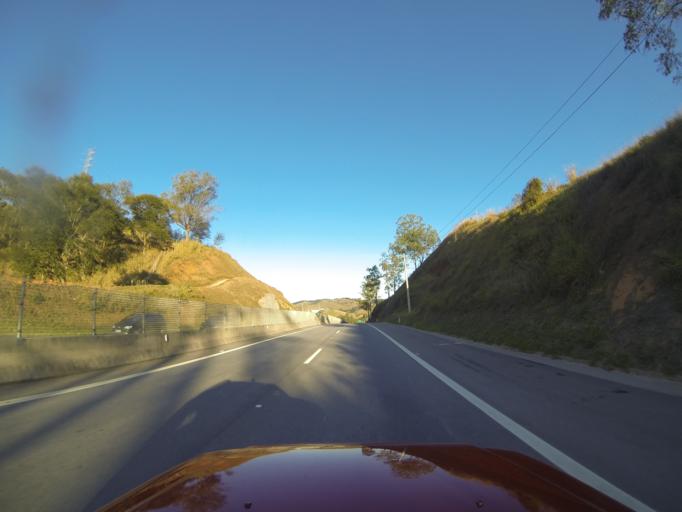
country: BR
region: Sao Paulo
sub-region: Santa Branca
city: Santa Branca
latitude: -23.3201
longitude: -45.7466
